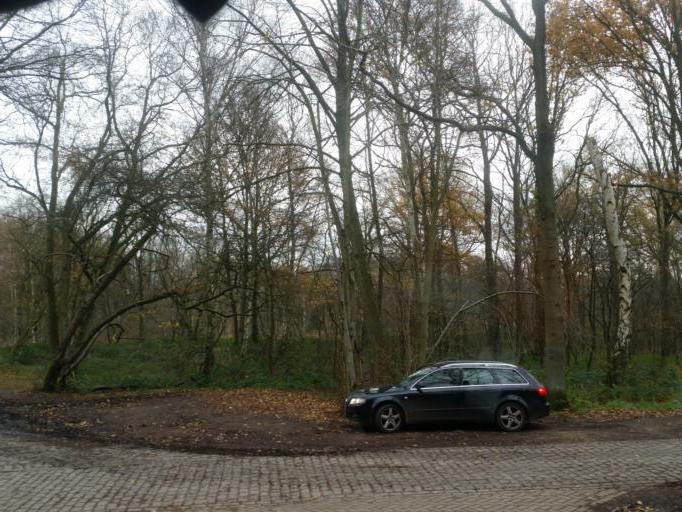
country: BE
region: Flanders
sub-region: Provincie Antwerpen
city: Brasschaat
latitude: 51.3279
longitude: 4.4942
